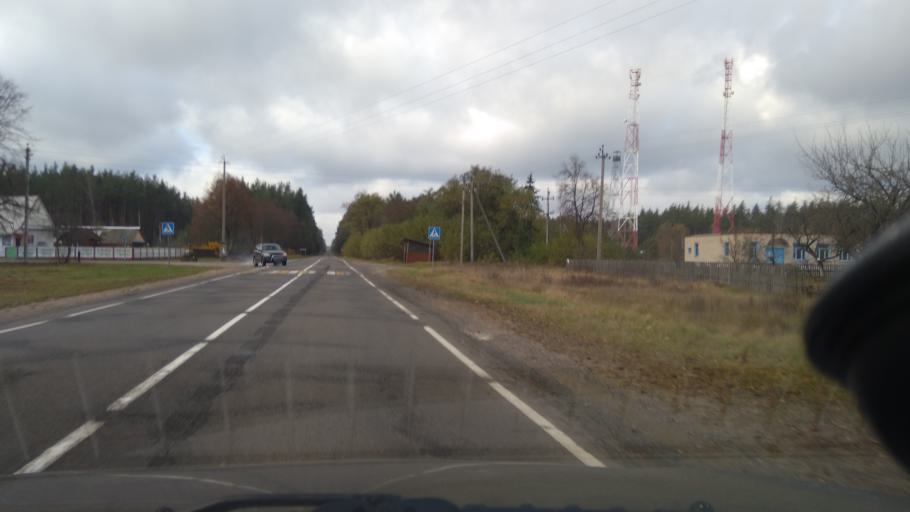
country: BY
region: Minsk
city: Slutsk
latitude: 53.2090
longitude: 27.7635
